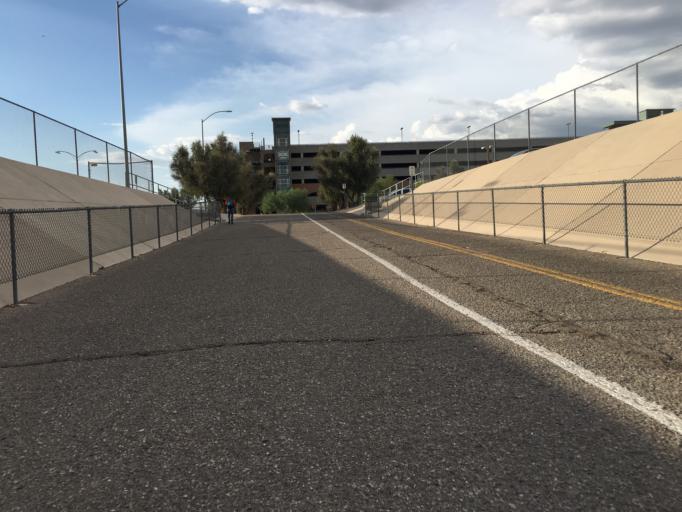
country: US
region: Arizona
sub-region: Pima County
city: Tucson
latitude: 32.2363
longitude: -110.9509
